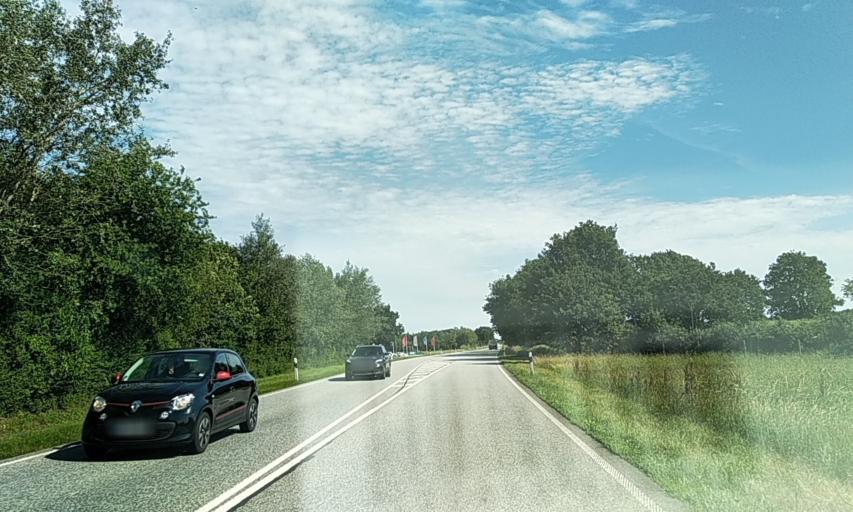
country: DE
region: Schleswig-Holstein
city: Kropp
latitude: 54.4172
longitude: 9.5297
